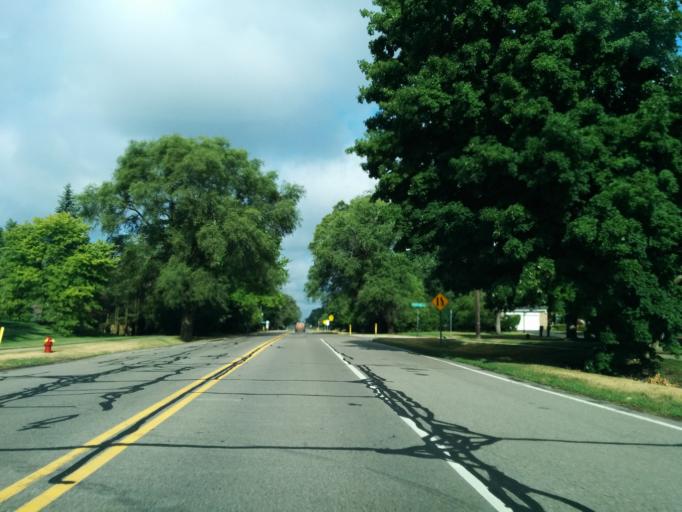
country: US
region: Michigan
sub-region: Oakland County
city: Franklin
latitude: 42.5289
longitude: -83.3438
